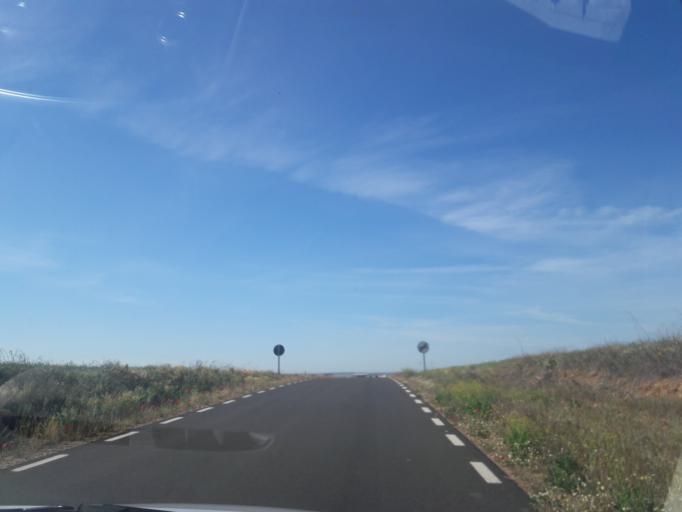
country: ES
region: Castille and Leon
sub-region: Provincia de Salamanca
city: Parada de Rubiales
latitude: 41.1358
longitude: -5.4304
